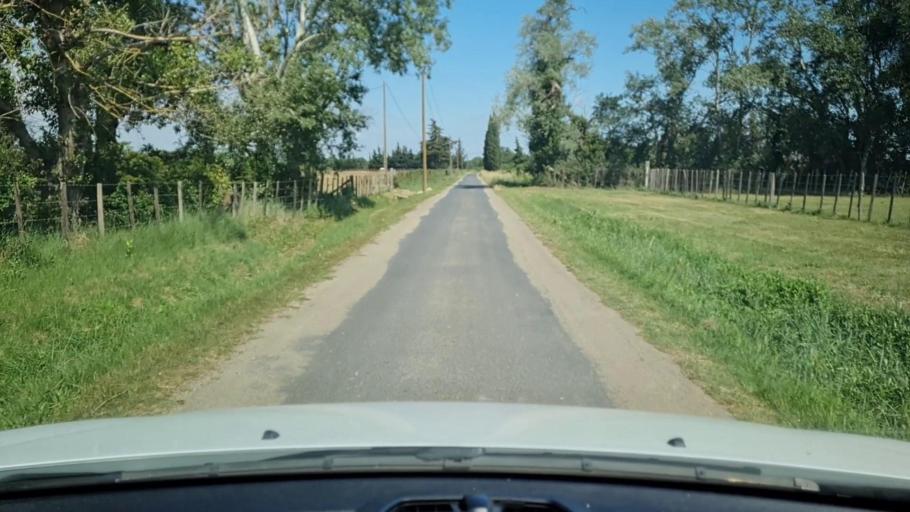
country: FR
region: Languedoc-Roussillon
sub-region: Departement du Gard
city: Le Cailar
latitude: 43.6516
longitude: 4.2393
